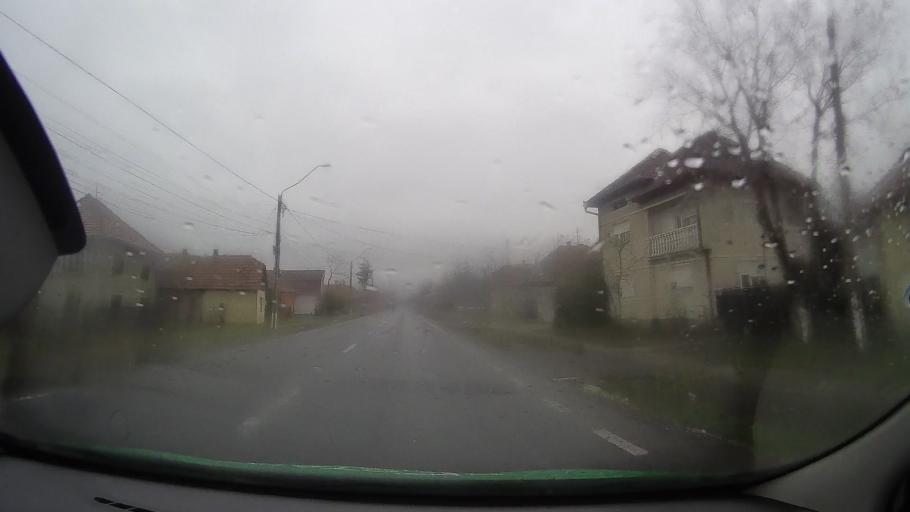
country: RO
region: Mures
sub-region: Comuna Suseni
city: Suseni
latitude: 46.8081
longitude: 24.7278
